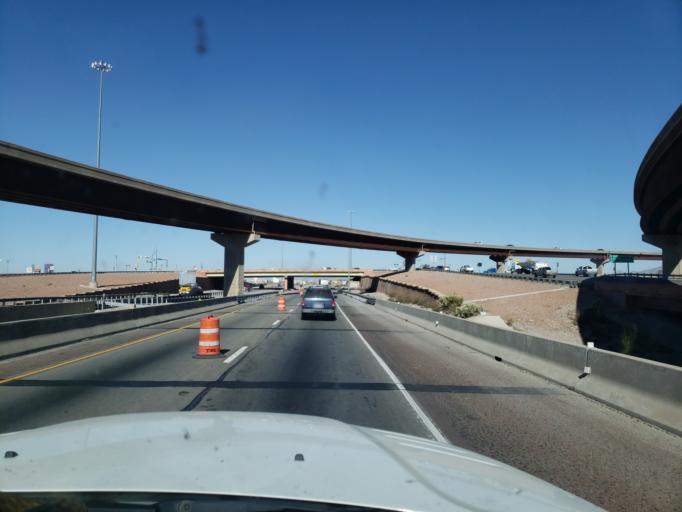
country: US
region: Texas
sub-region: El Paso County
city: Canutillo
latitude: 31.9064
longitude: -106.5827
